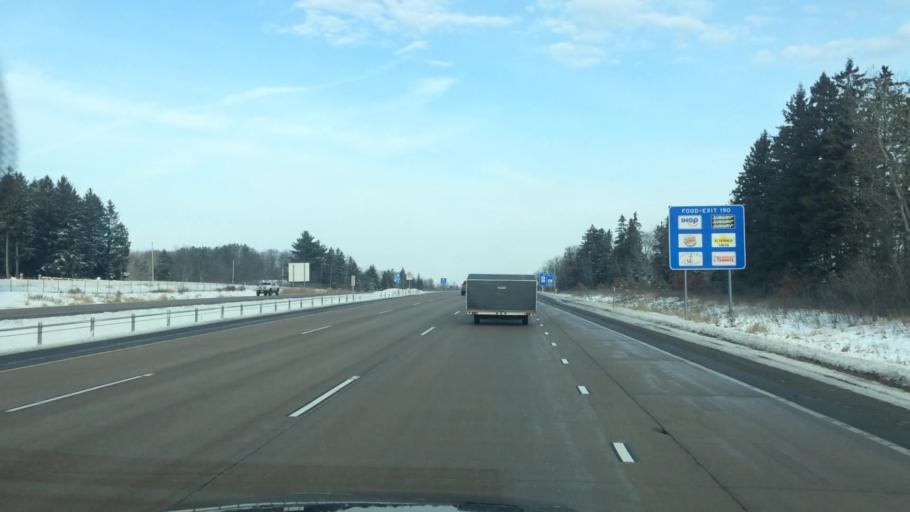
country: US
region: Wisconsin
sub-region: Marathon County
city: Rib Mountain
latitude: 44.9171
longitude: -89.6546
